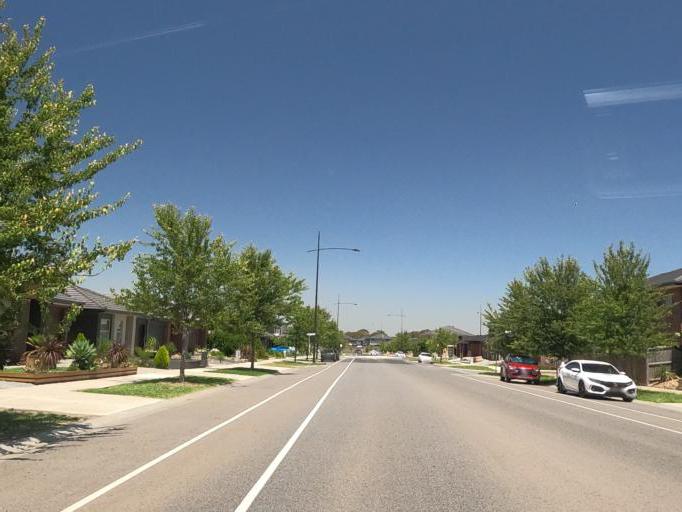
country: AU
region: Victoria
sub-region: Hume
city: Greenvale
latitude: -37.6247
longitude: 144.8782
